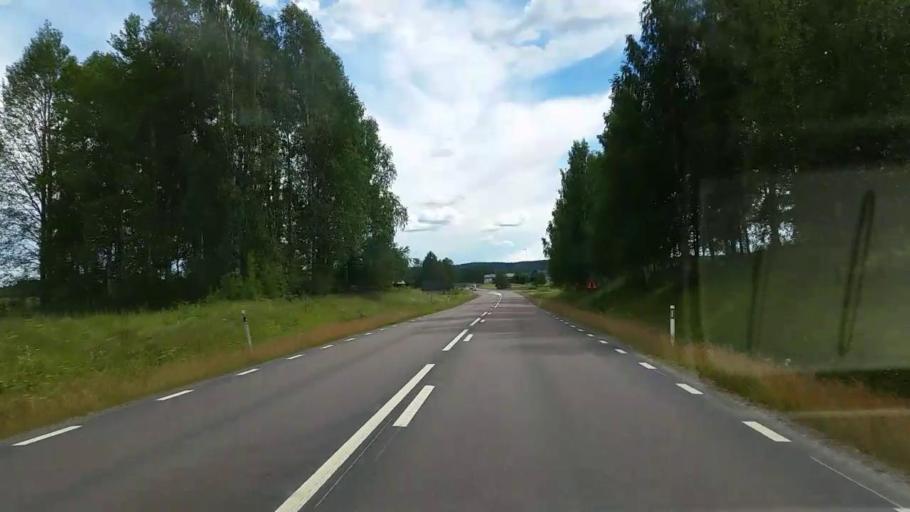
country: SE
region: Gaevleborg
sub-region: Ovanakers Kommun
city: Edsbyn
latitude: 61.3791
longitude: 15.8363
